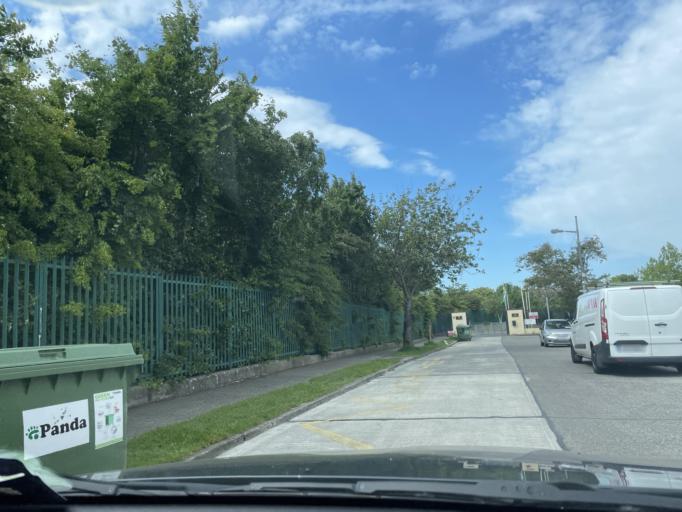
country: IE
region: Leinster
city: Donaghmede
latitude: 53.3961
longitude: -6.1599
